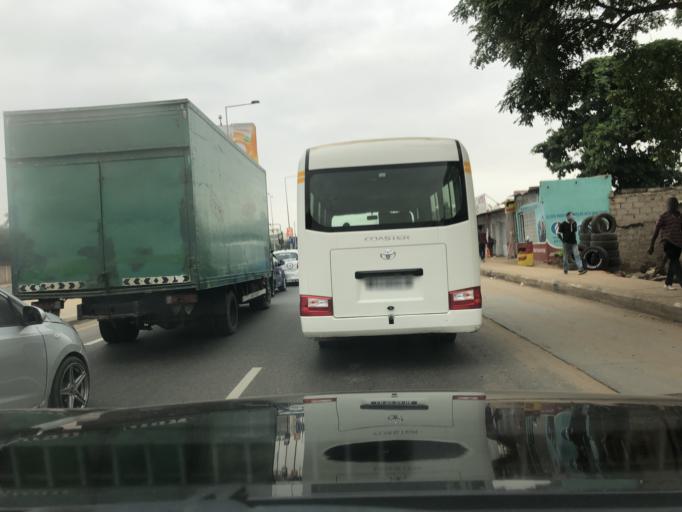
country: AO
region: Luanda
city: Luanda
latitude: -8.8533
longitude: 13.2810
